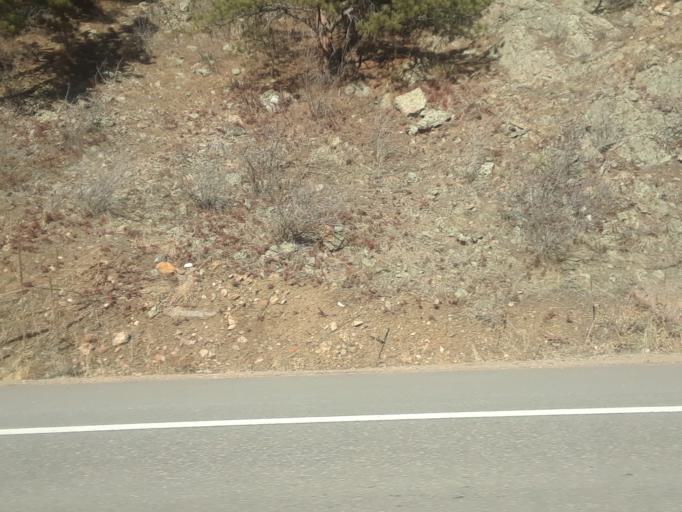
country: US
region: Colorado
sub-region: Boulder County
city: Boulder
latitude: 40.1089
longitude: -105.3352
